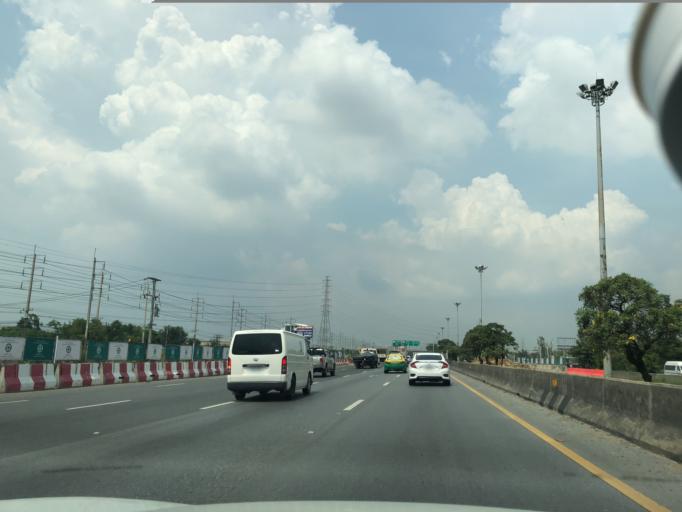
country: TH
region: Phra Nakhon Si Ayutthaya
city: Bang Pa-in
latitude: 14.1759
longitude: 100.6160
